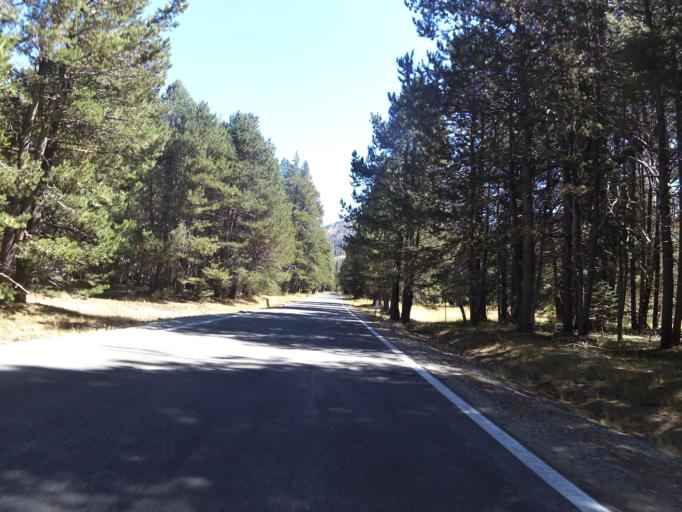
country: US
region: Nevada
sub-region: Douglas County
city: Gardnerville Ranchos
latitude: 38.5384
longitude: -119.8966
